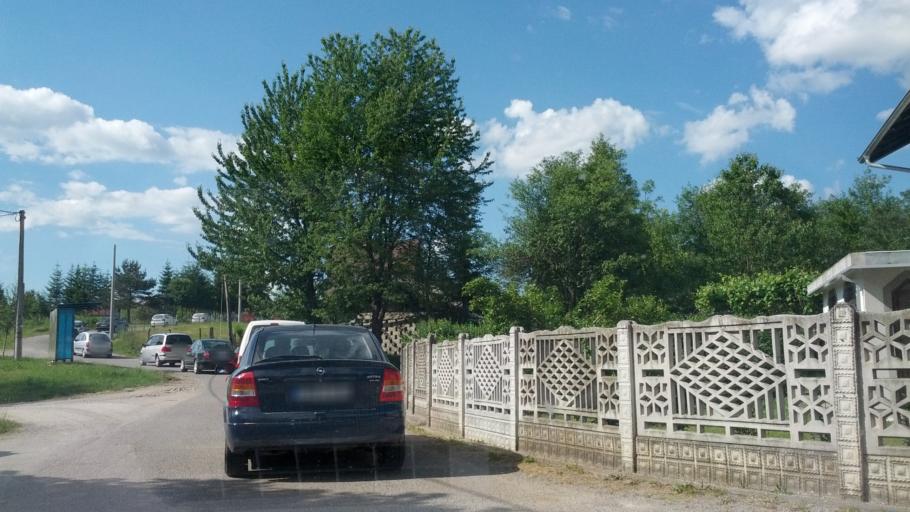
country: BA
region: Federation of Bosnia and Herzegovina
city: Ostrozac
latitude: 44.9236
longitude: 15.9568
